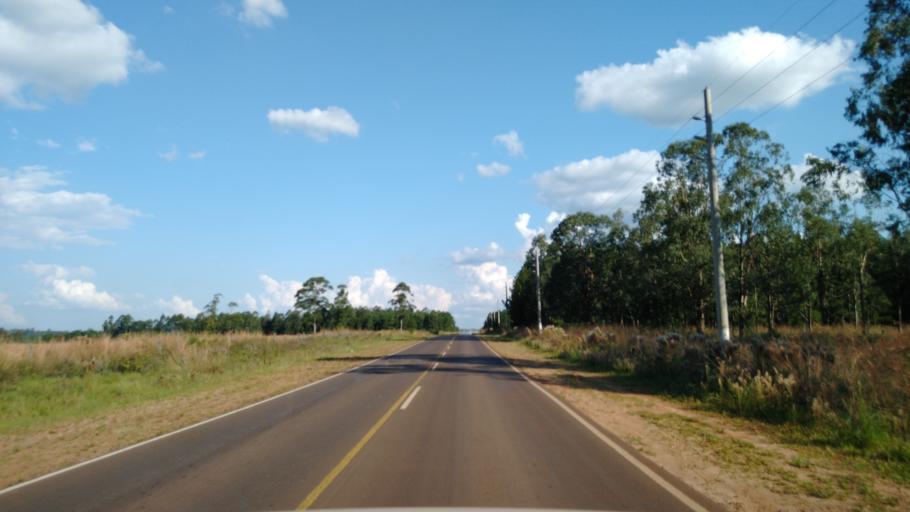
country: PY
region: Itapua
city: San Juan del Parana
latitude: -27.3778
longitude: -55.9920
